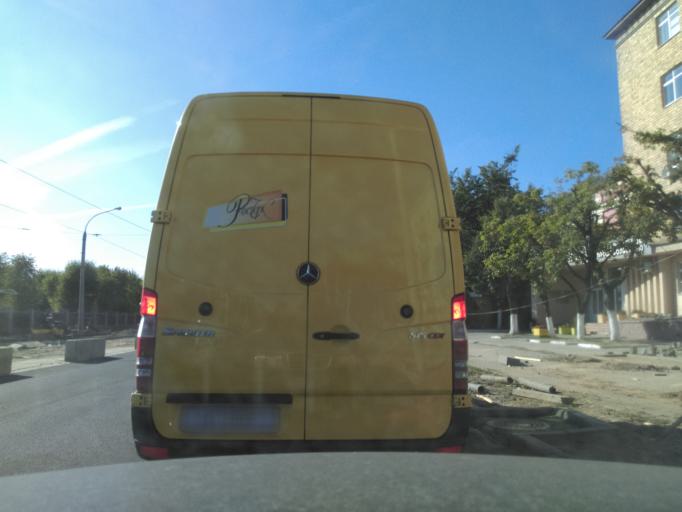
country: BY
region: Minsk
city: Minsk
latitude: 53.9043
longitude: 27.5971
